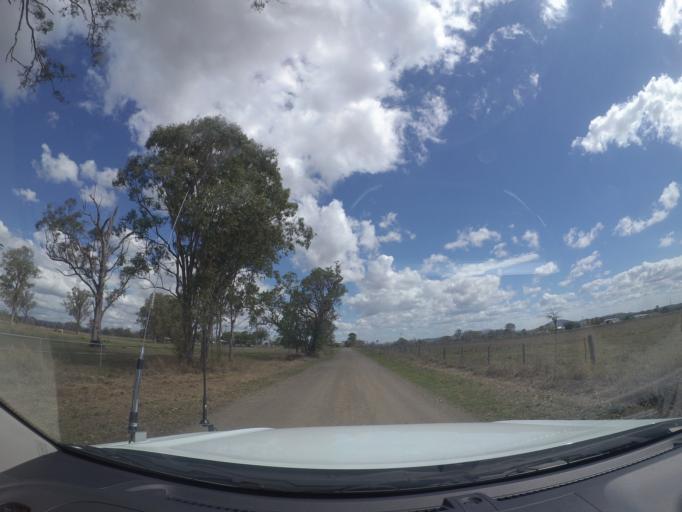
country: AU
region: Queensland
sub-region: Logan
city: Cedar Vale
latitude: -27.8948
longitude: 152.9588
